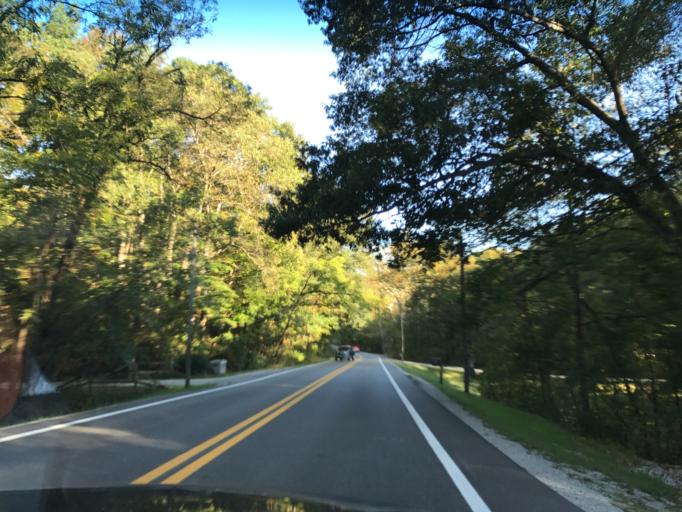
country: US
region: West Virginia
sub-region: Ritchie County
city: Harrisville
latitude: 39.2769
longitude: -81.0706
